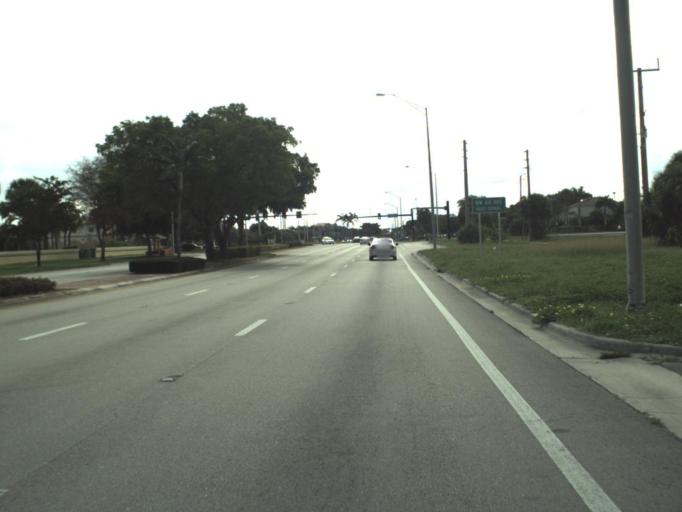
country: US
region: Florida
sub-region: Broward County
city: Lauderdale Lakes
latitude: 26.1646
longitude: -80.2374
